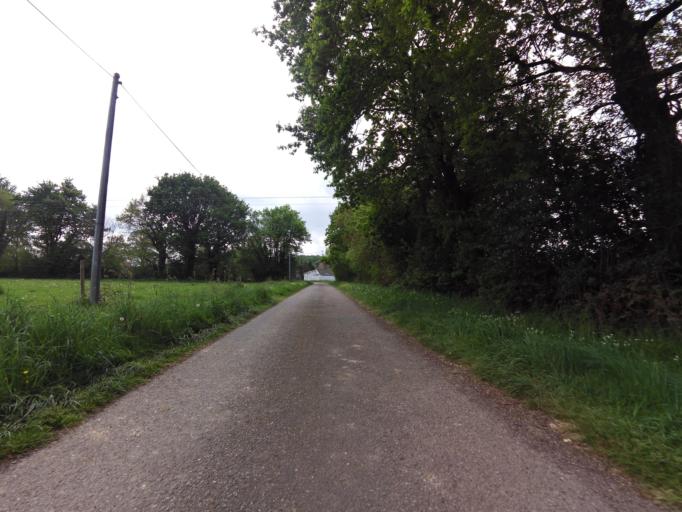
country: FR
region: Brittany
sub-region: Departement du Morbihan
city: Saint-Martin-sur-Oust
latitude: 47.7284
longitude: -2.2747
